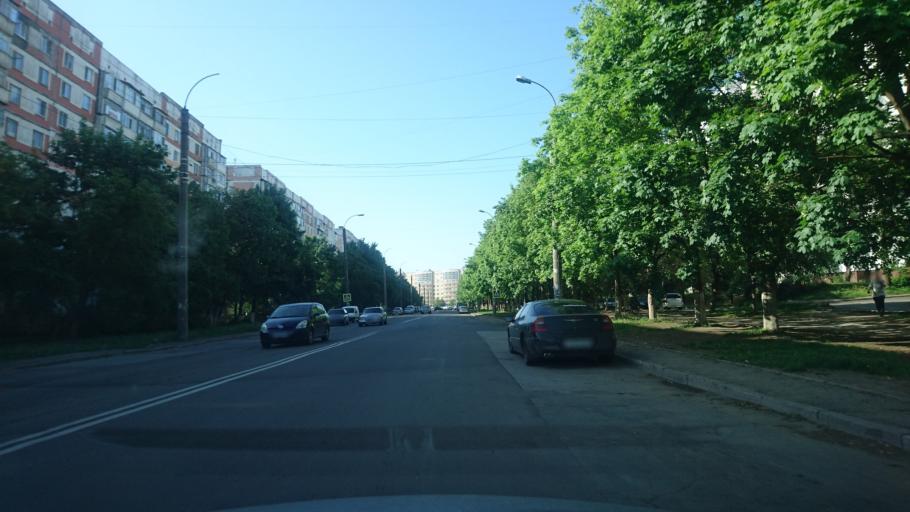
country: MD
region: Chisinau
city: Vatra
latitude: 47.0420
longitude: 28.7701
